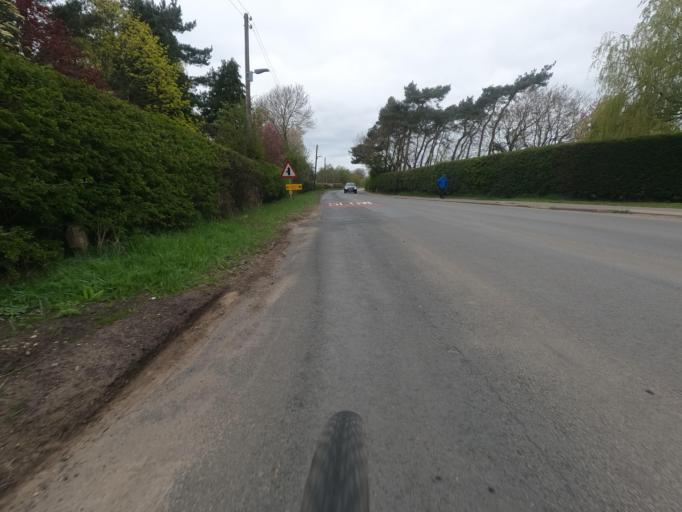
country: GB
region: England
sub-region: Northumberland
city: Ponteland
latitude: 55.0595
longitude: -1.7495
